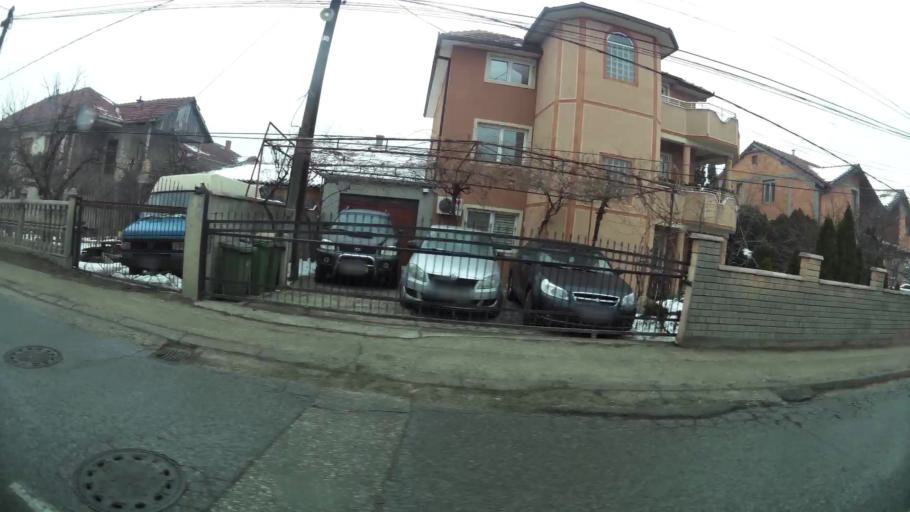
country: MK
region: Saraj
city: Saraj
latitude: 42.0222
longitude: 21.3505
